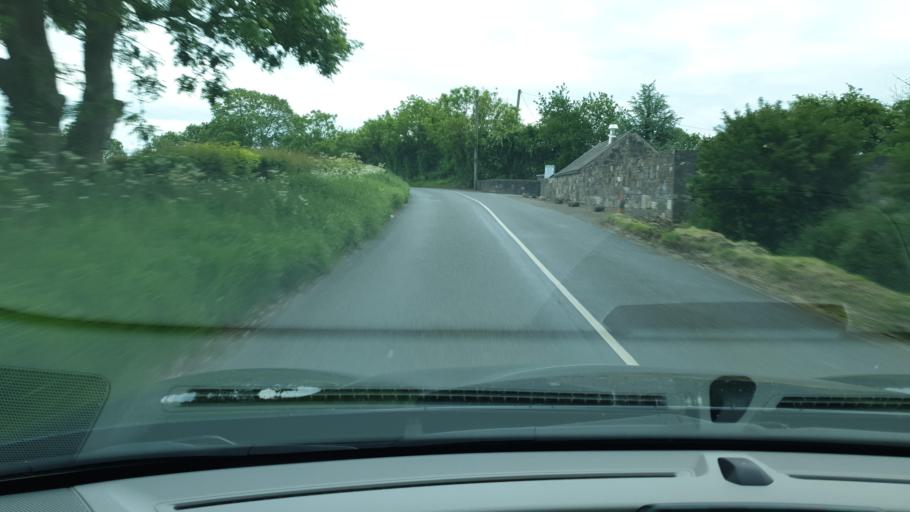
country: IE
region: Leinster
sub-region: An Mhi
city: Ashbourne
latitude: 53.5580
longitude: -6.3340
